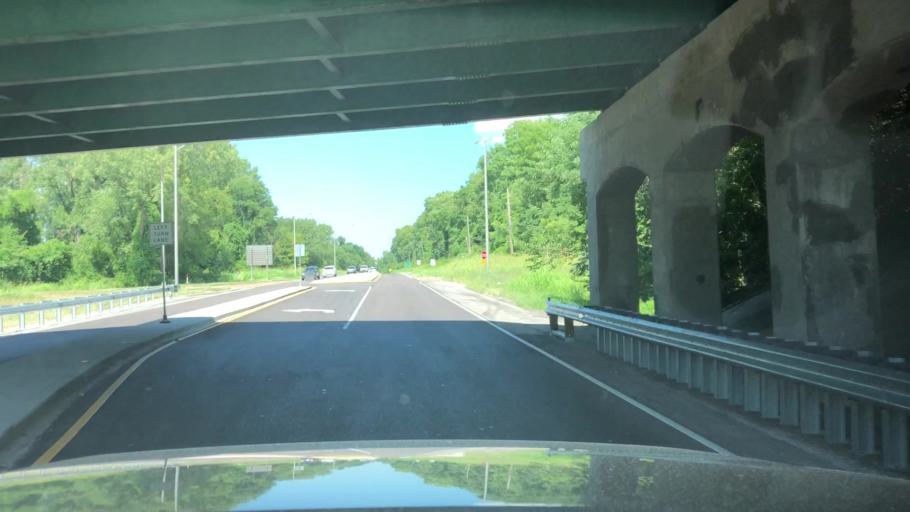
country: US
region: Illinois
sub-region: Saint Clair County
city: Alorton
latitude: 38.5676
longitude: -90.0914
